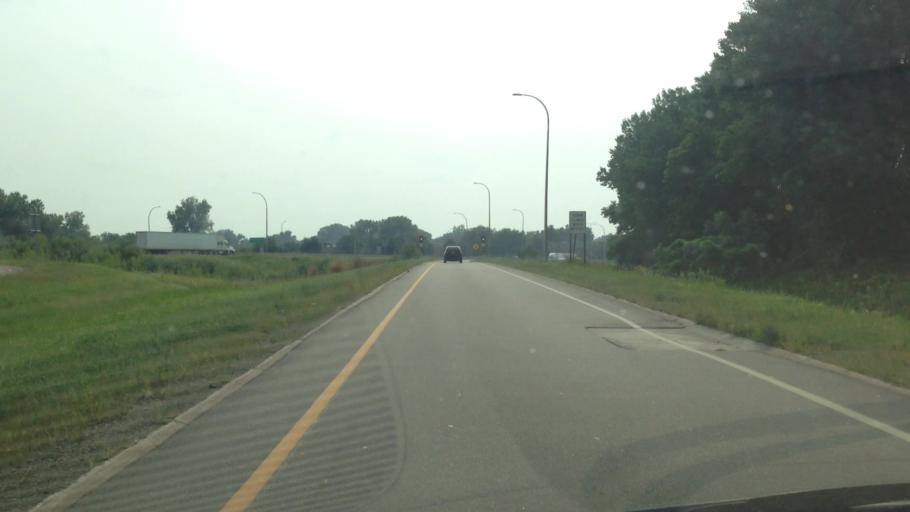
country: US
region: Minnesota
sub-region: Ramsey County
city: New Brighton
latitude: 45.0683
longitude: -93.1874
